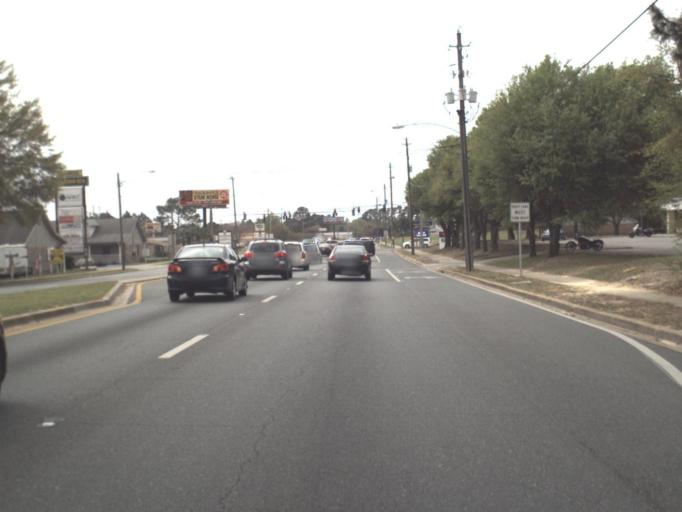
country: US
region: Florida
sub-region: Okaloosa County
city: Crestview
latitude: 30.7456
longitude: -86.5640
